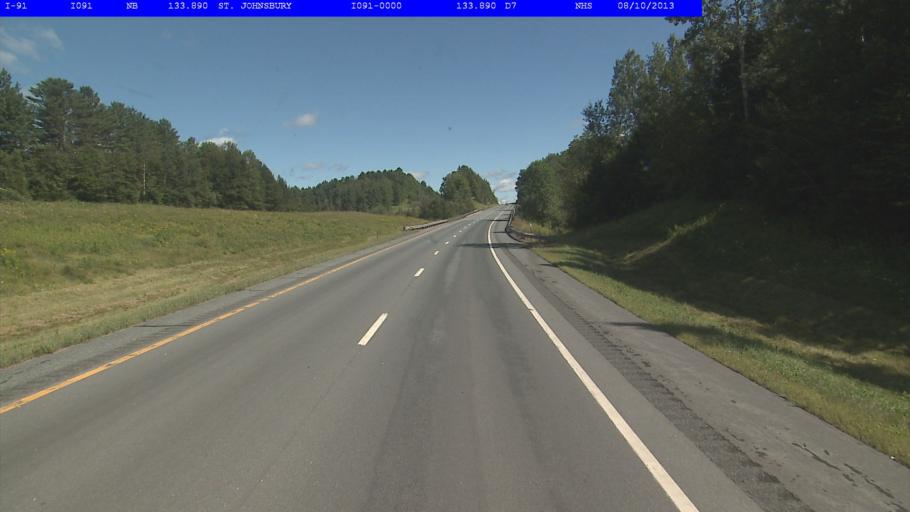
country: US
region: Vermont
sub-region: Caledonia County
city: Lyndon
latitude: 44.4729
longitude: -72.0248
